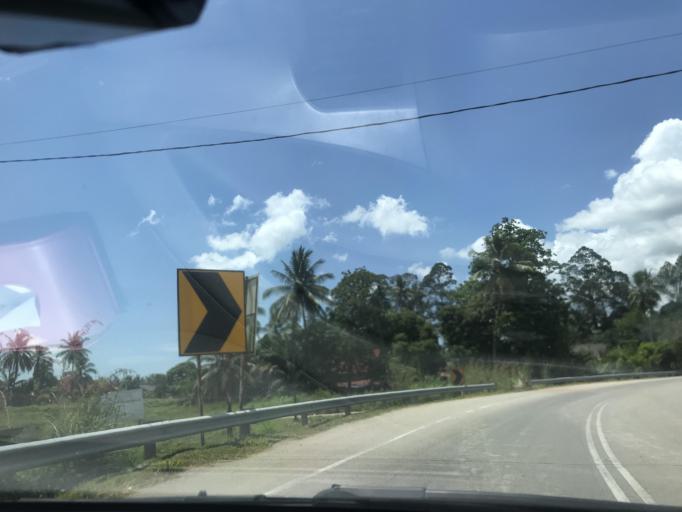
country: MY
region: Kelantan
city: Tumpat
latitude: 6.2015
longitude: 102.1232
